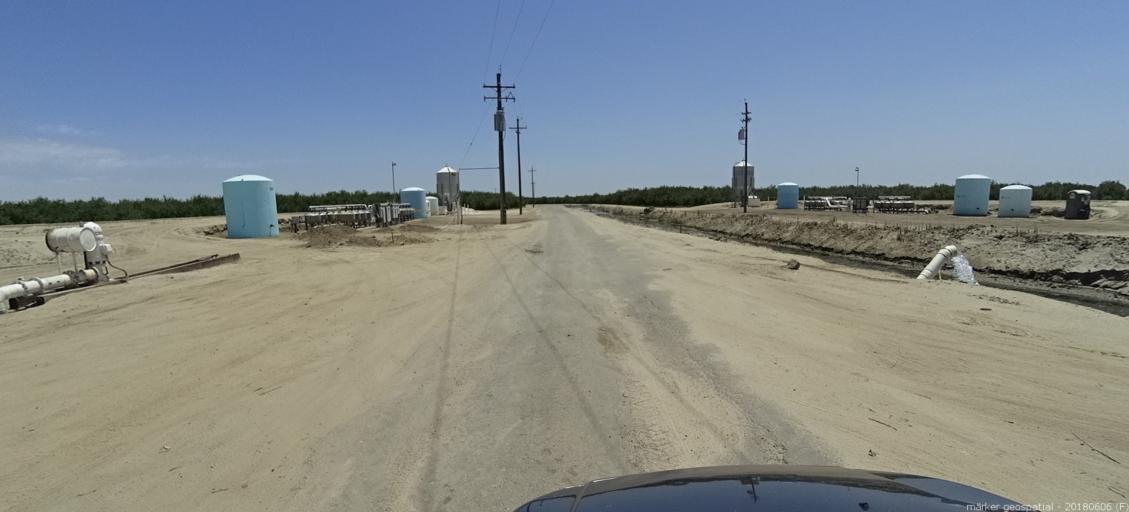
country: US
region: California
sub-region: Fresno County
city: Mendota
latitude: 36.7921
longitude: -120.3215
